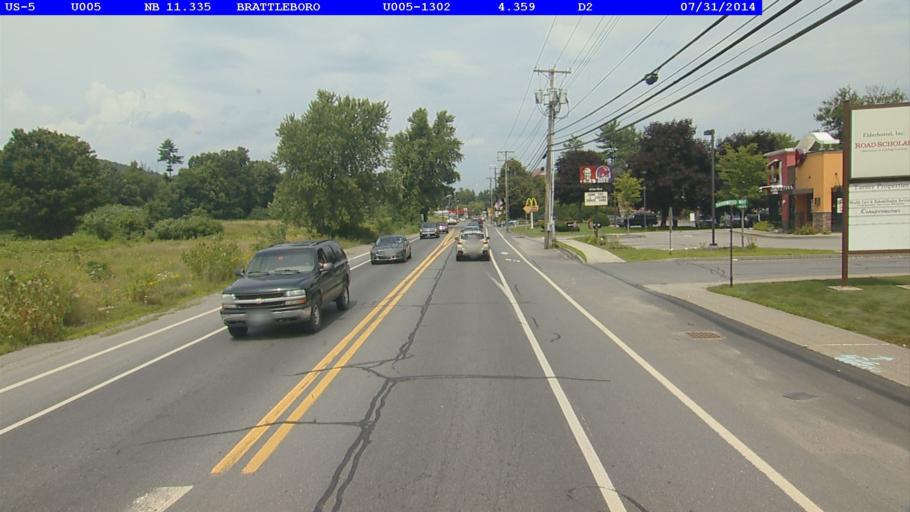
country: US
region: Vermont
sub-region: Windham County
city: Brattleboro
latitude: 42.8815
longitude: -72.5585
